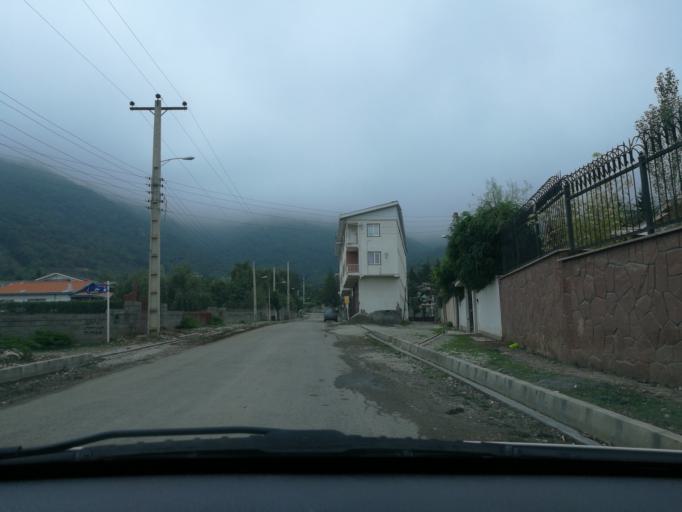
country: IR
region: Mazandaran
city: `Abbasabad
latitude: 36.4983
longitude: 51.2162
